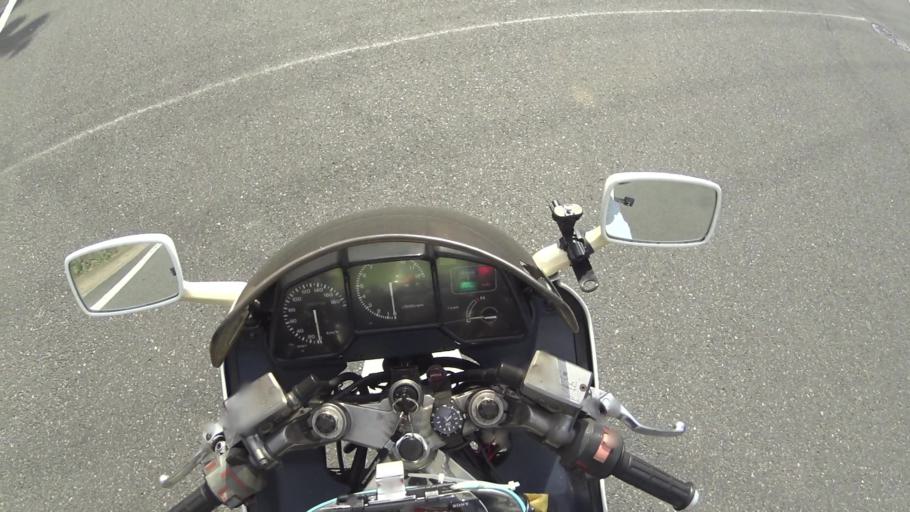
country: JP
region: Kyoto
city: Miyazu
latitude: 35.6421
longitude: 135.0908
